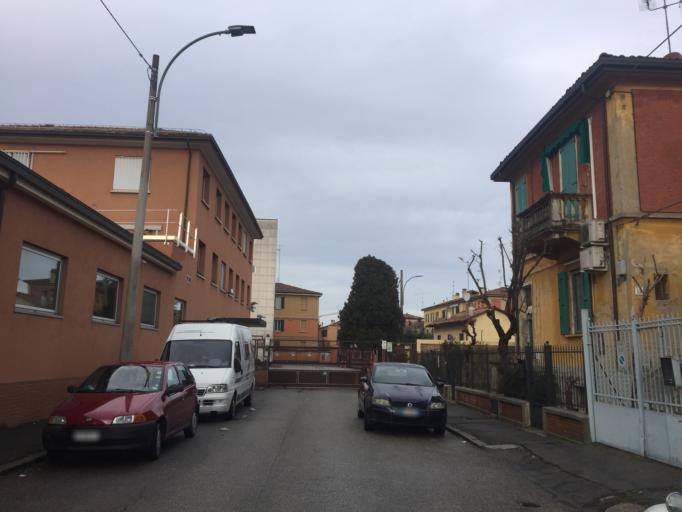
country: IT
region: Emilia-Romagna
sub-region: Provincia di Bologna
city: Casalecchio di Reno
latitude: 44.5053
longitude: 11.2998
